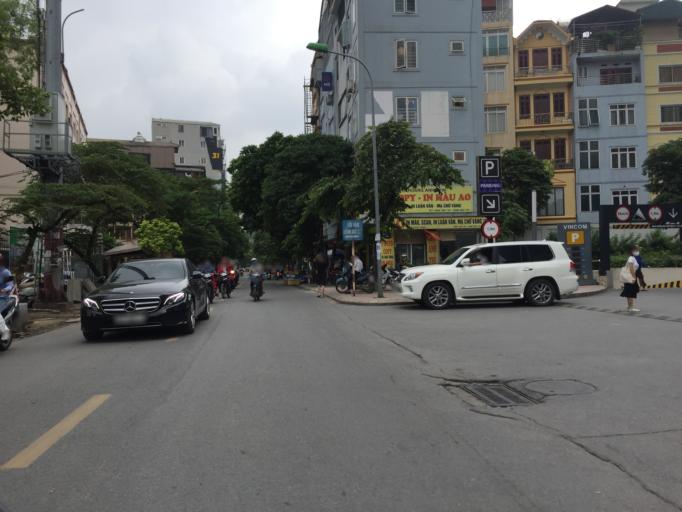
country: VN
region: Ha Noi
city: Cau Giay
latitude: 21.0230
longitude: 105.8089
